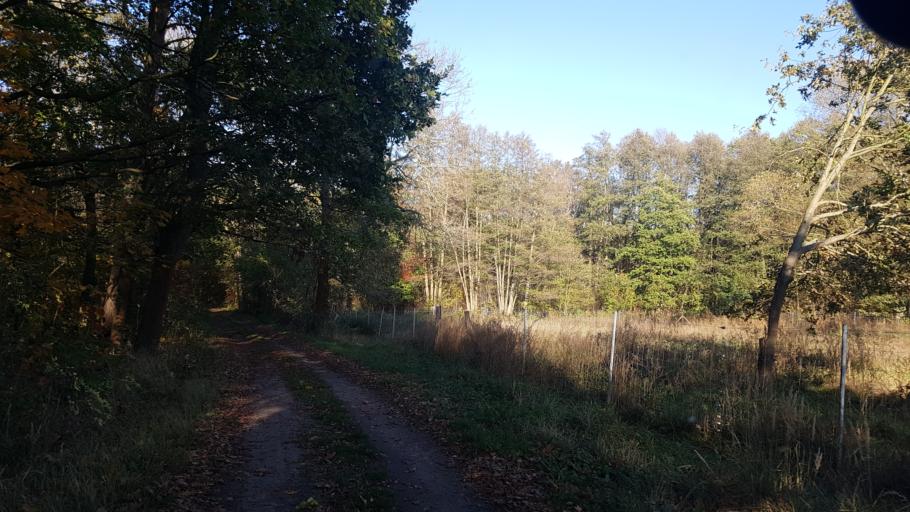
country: DE
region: Brandenburg
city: Doberlug-Kirchhain
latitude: 51.6380
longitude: 13.5340
